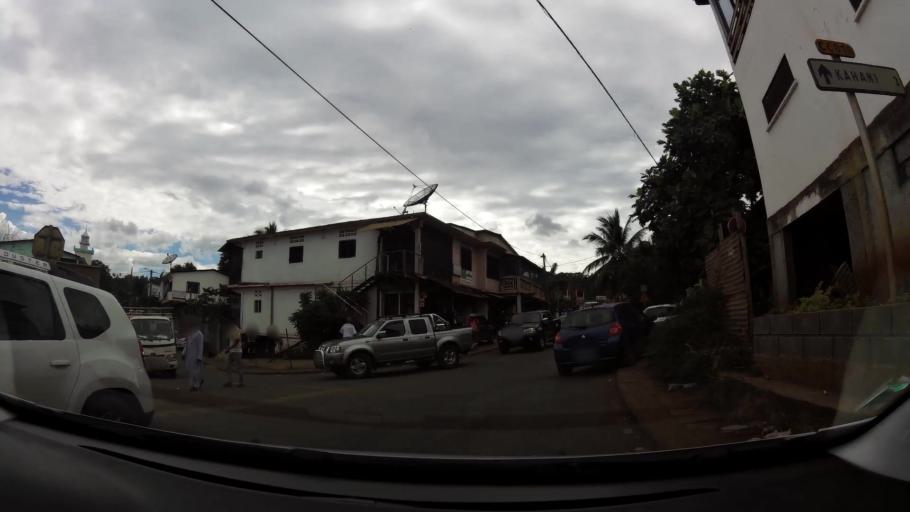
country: YT
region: Chiconi
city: Chiconi
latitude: -12.8336
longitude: 45.1139
